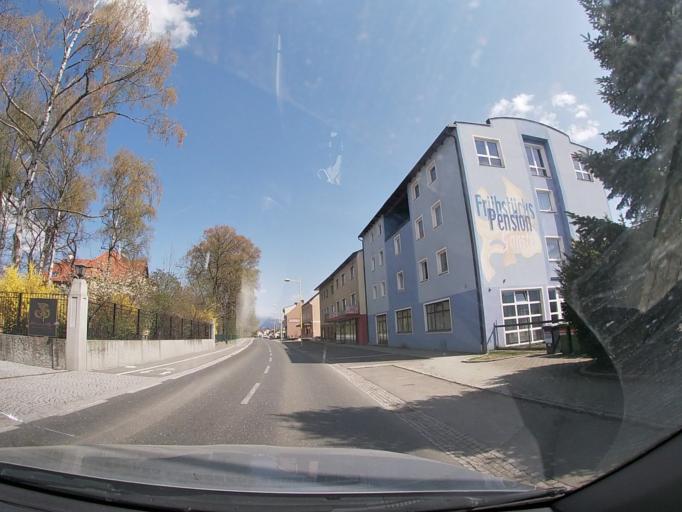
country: AT
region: Styria
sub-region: Politischer Bezirk Murtal
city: Zeltweg
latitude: 47.1906
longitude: 14.7473
